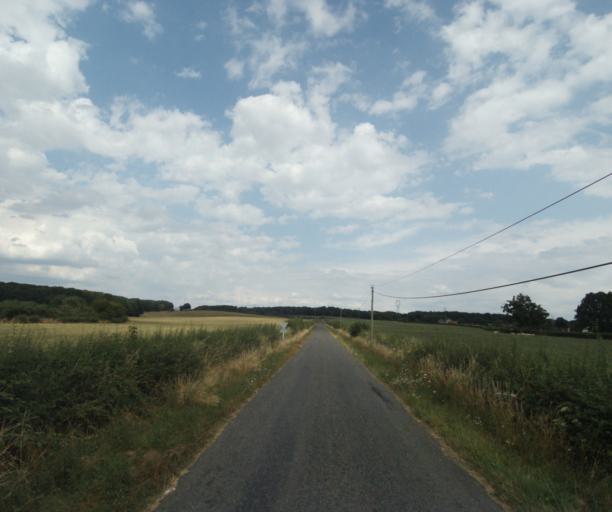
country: FR
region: Bourgogne
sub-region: Departement de Saone-et-Loire
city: Gueugnon
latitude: 46.6155
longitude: 4.0798
